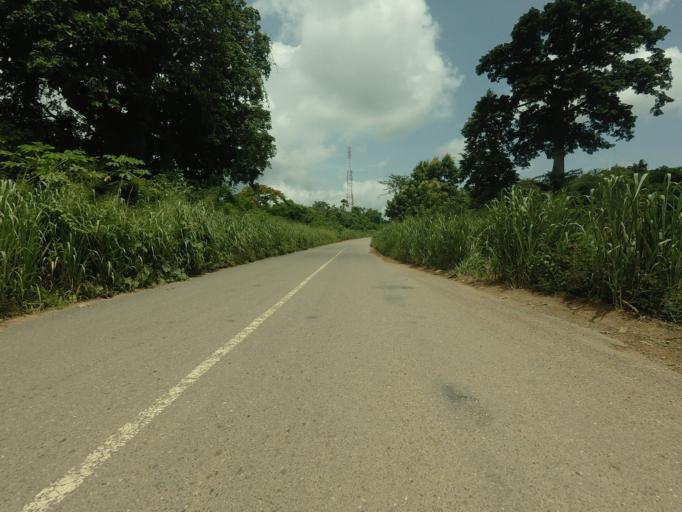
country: GH
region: Volta
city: Ho
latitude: 6.7184
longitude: 0.3395
